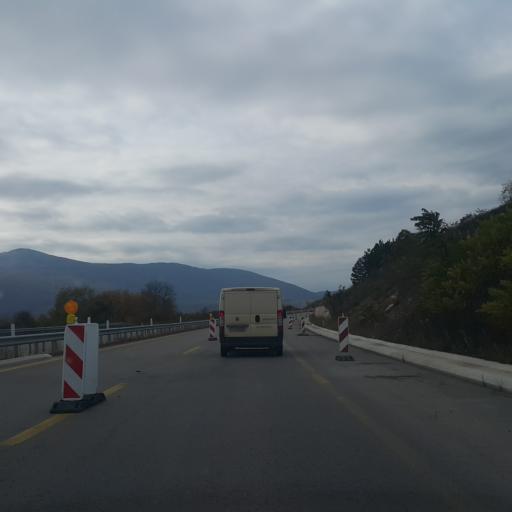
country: RS
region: Central Serbia
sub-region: Pirotski Okrug
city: Bela Palanka
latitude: 43.2356
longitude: 22.3562
